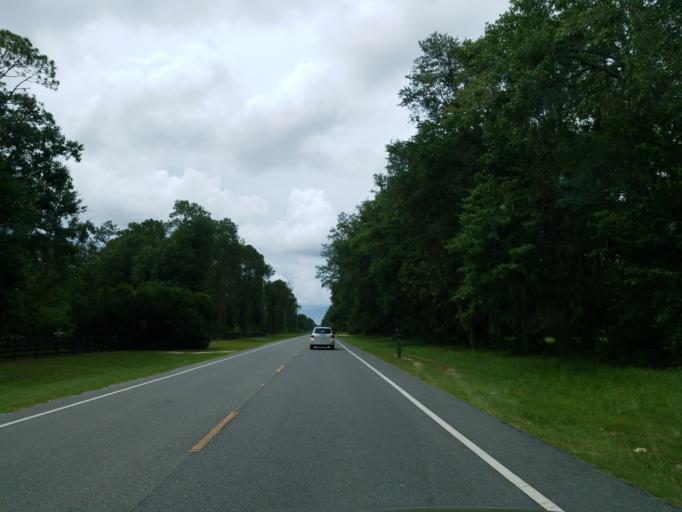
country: US
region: Florida
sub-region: Alachua County
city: High Springs
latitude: 29.8985
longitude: -82.4973
